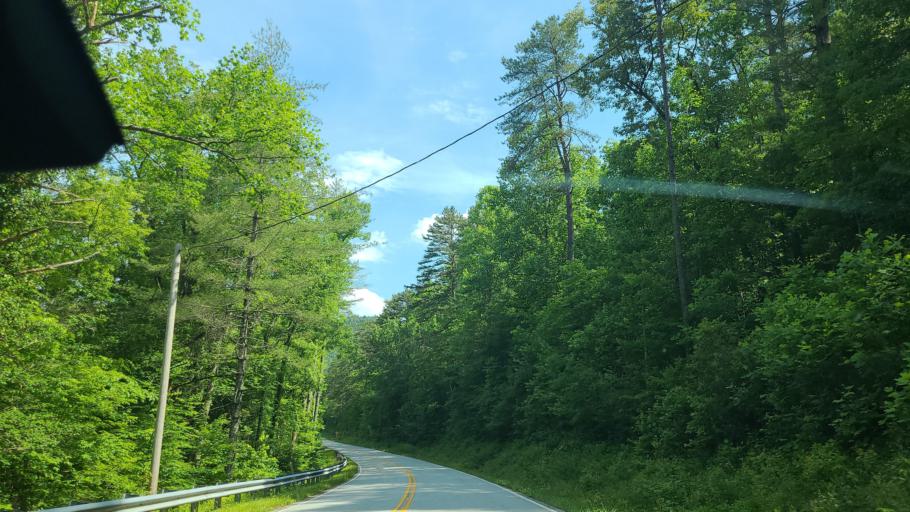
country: US
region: South Carolina
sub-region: Oconee County
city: Walhalla
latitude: 34.9047
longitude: -83.1802
